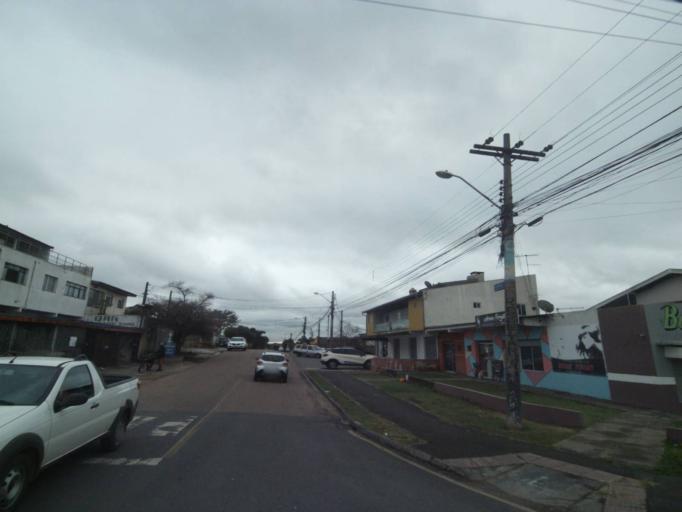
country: BR
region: Parana
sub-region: Curitiba
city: Curitiba
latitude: -25.5179
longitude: -49.3044
